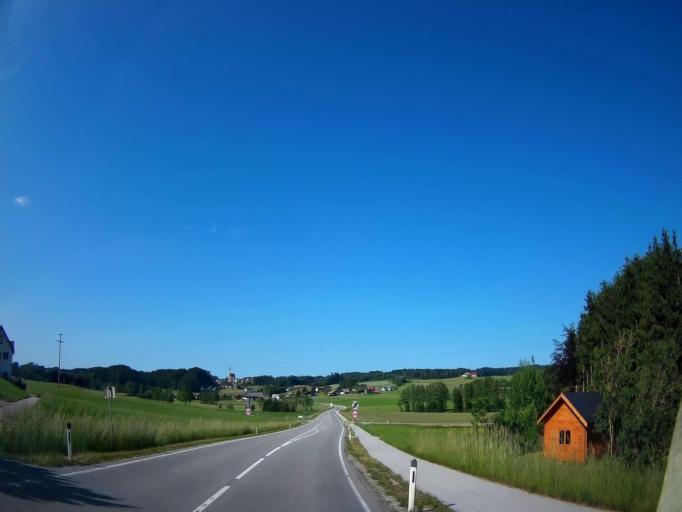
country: AT
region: Salzburg
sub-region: Politischer Bezirk Salzburg-Umgebung
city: Dorfbeuern
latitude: 48.0564
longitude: 12.9843
